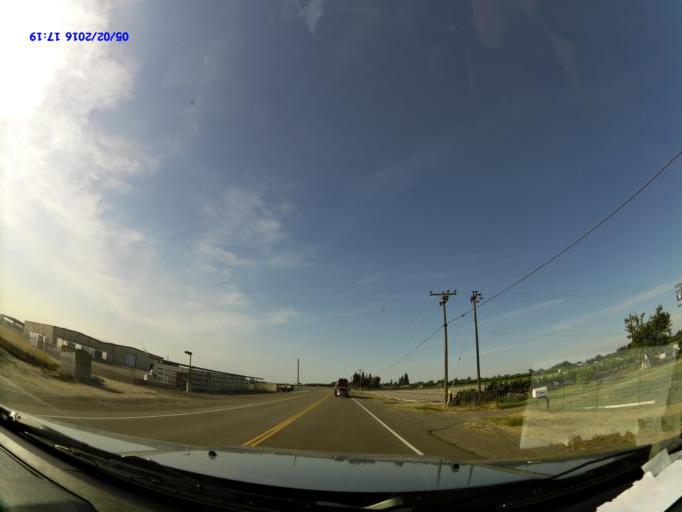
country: US
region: California
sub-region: San Joaquin County
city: Manteca
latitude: 37.8298
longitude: -121.1445
